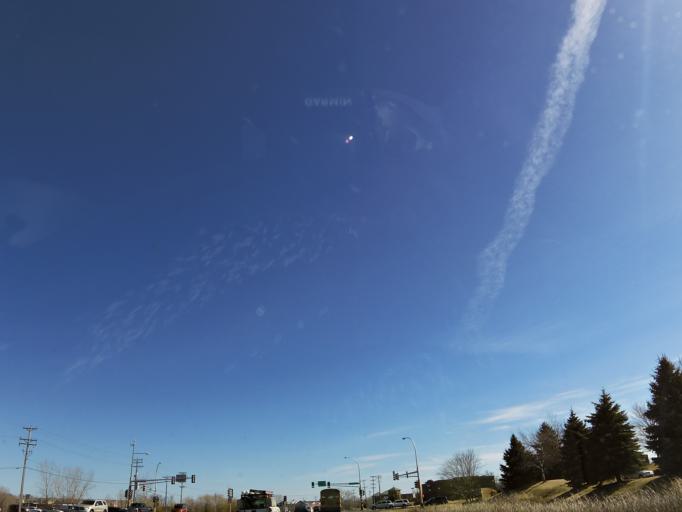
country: US
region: Minnesota
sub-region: Hennepin County
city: Plymouth
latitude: 45.0227
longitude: -93.4941
